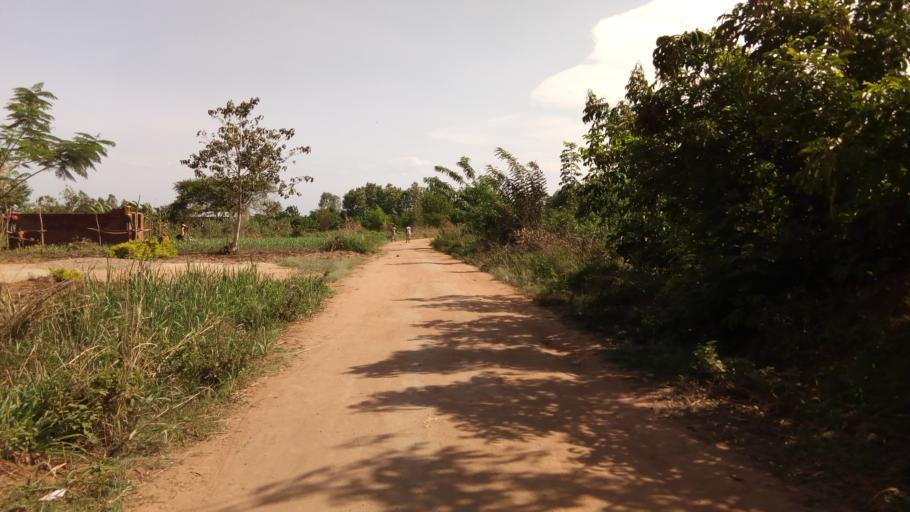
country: UG
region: Northern Region
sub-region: Gulu District
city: Gulu
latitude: 2.7965
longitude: 32.3276
